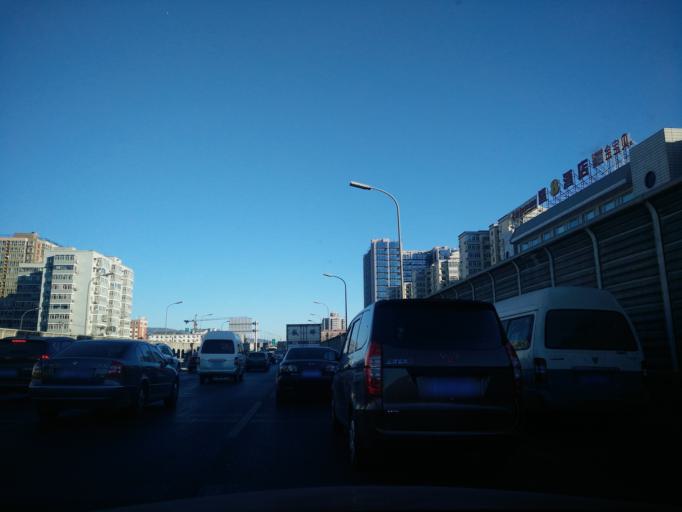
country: CN
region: Beijing
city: Lugu
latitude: 39.8985
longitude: 116.2052
